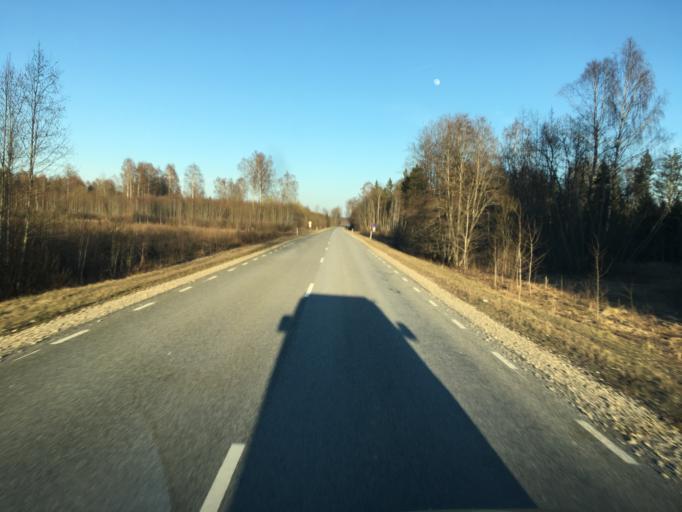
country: EE
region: Raplamaa
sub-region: Rapla vald
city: Rapla
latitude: 59.0756
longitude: 24.8763
